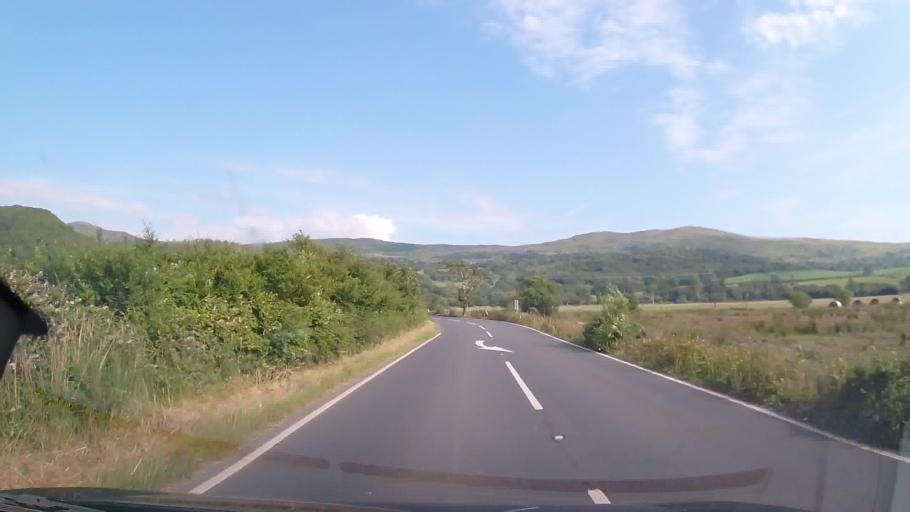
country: GB
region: Wales
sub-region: Gwynedd
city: Penrhyndeudraeth
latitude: 52.8937
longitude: -4.0779
